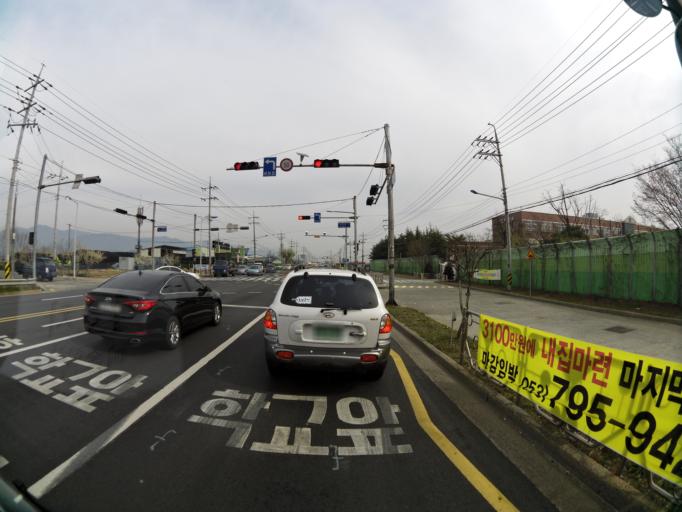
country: KR
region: Gyeongsangbuk-do
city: Gyeongsan-si
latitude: 35.8615
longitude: 128.7719
